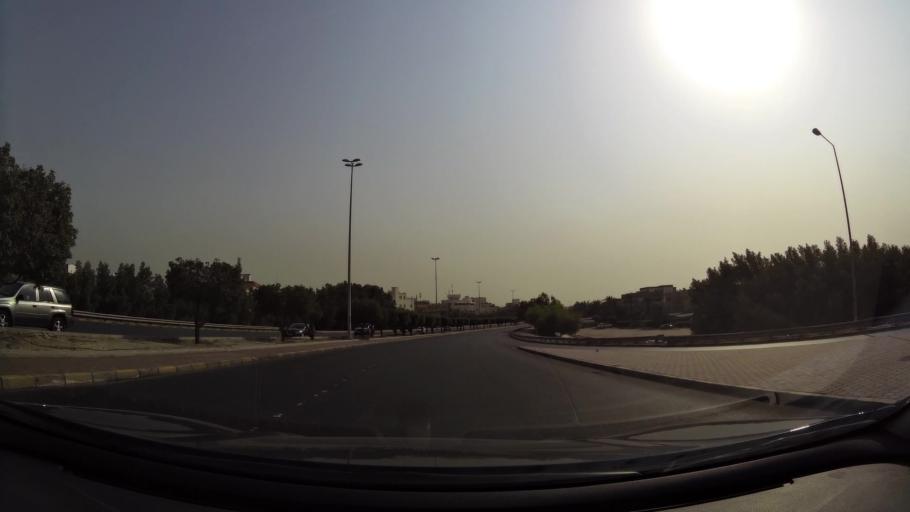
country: KW
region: Mubarak al Kabir
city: Sabah as Salim
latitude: 29.2638
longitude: 48.0669
